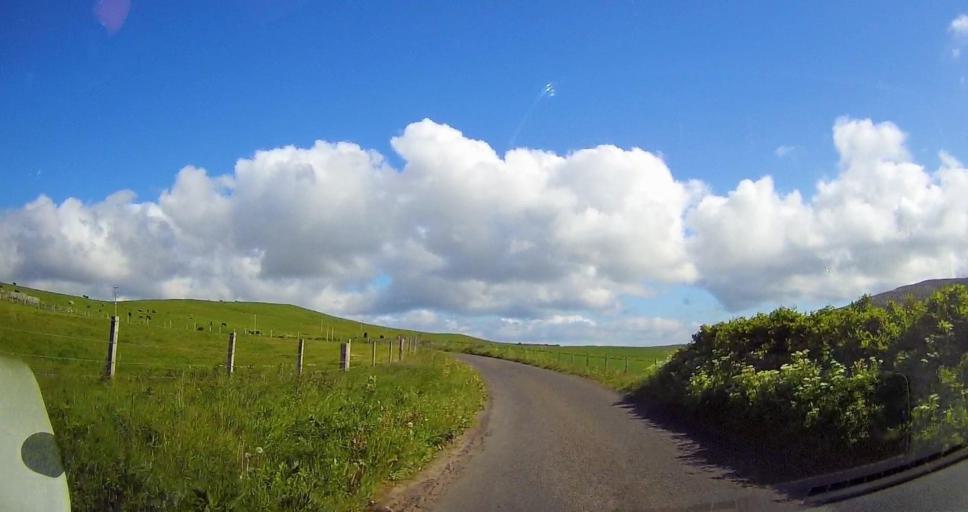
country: GB
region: Scotland
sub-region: Orkney Islands
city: Stromness
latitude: 58.9825
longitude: -3.1400
